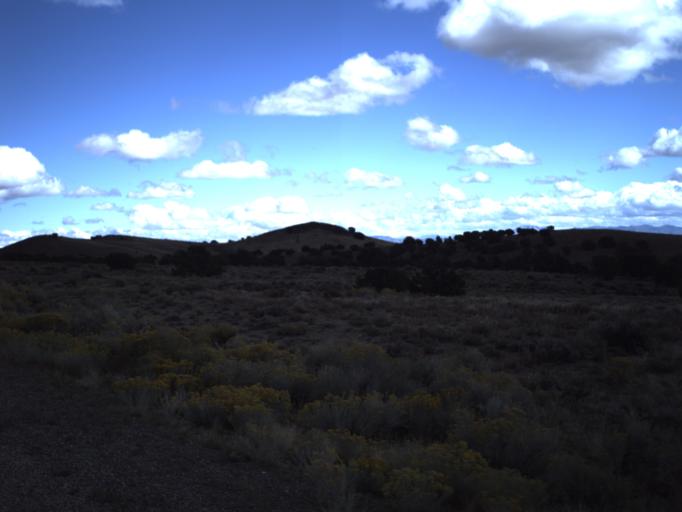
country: US
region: Utah
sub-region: Beaver County
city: Milford
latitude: 38.4578
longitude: -113.2564
